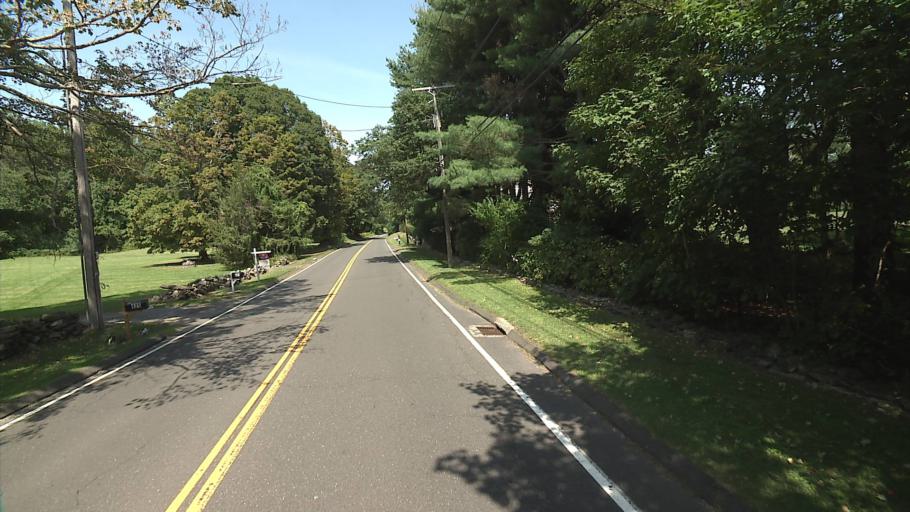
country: US
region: Connecticut
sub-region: Fairfield County
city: Westport
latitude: 41.2340
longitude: -73.3214
